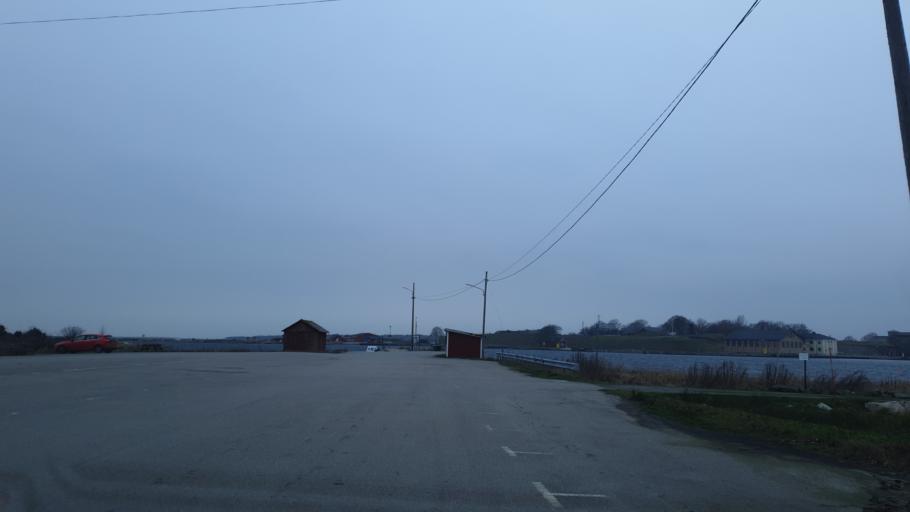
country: SE
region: Blekinge
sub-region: Karlskrona Kommun
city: Karlskrona
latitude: 56.1058
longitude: 15.5967
